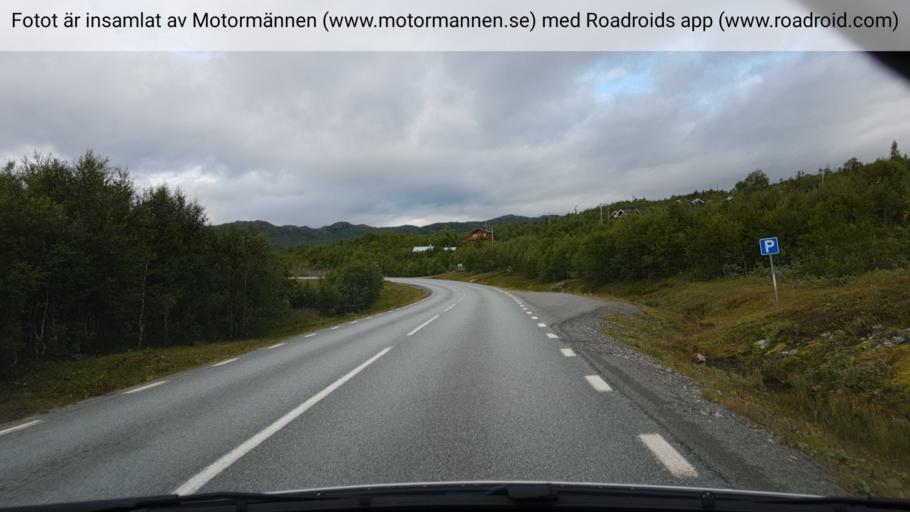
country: NO
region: Nordland
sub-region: Rana
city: Mo i Rana
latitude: 66.1252
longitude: 14.6626
